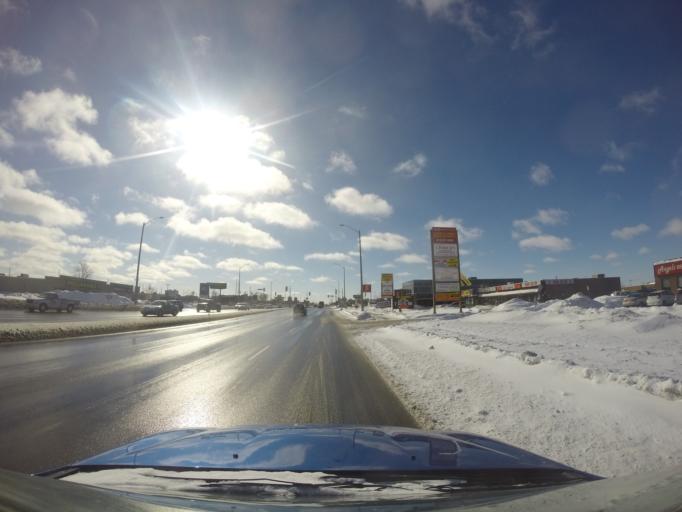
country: CA
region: Ontario
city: Cambridge
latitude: 43.4027
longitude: -80.3265
